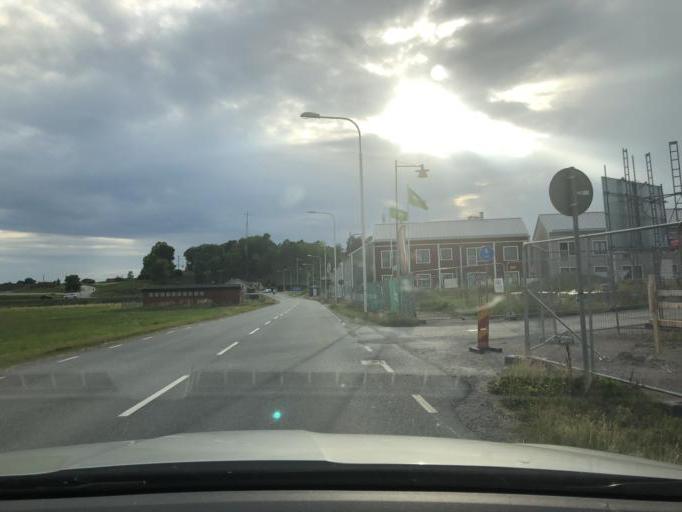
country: SE
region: Soedermanland
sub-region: Strangnas Kommun
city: Mariefred
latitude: 59.2618
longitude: 17.2180
